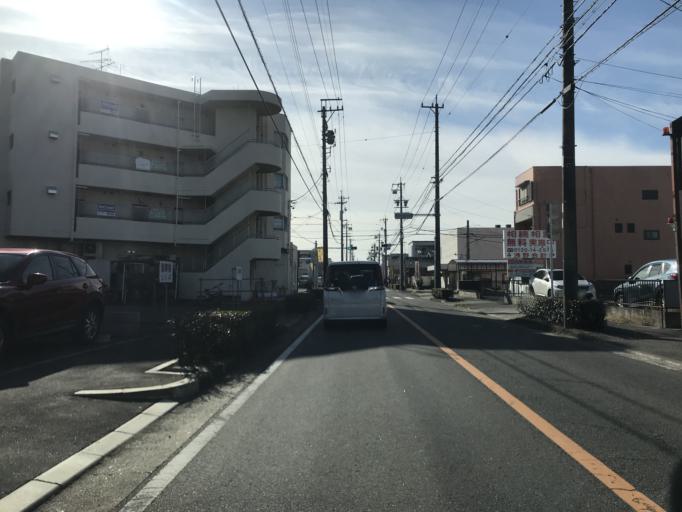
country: JP
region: Aichi
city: Inazawa
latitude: 35.2098
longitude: 136.8335
